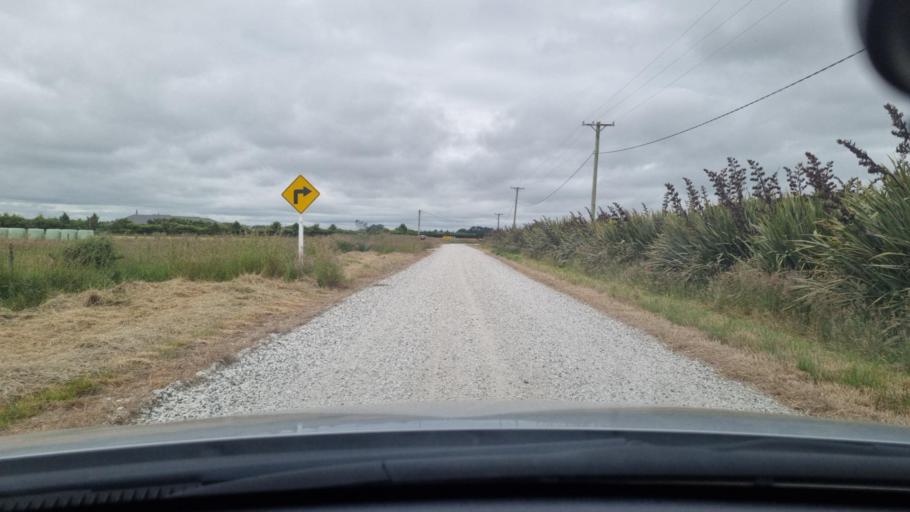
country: NZ
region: Southland
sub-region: Invercargill City
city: Invercargill
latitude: -46.3800
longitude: 168.2872
